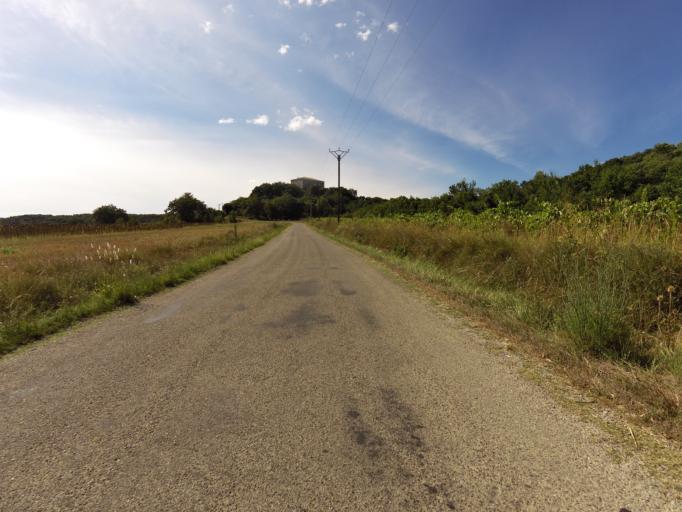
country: FR
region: Languedoc-Roussillon
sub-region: Departement du Gard
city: Lezan
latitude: 43.9770
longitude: 4.0241
